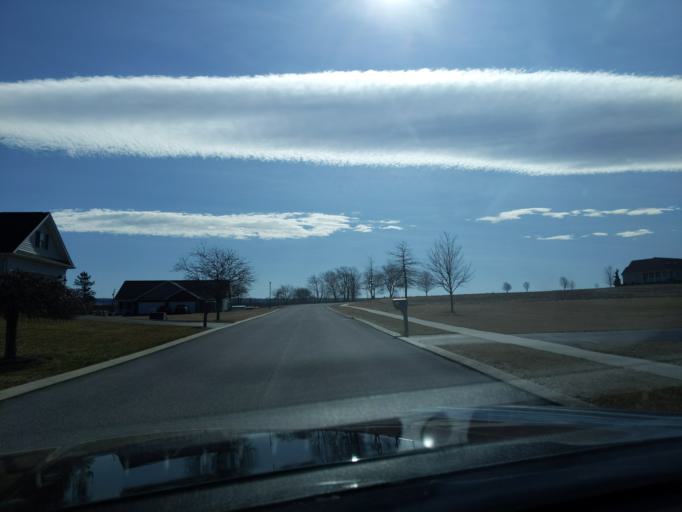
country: US
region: Pennsylvania
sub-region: Blair County
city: Martinsburg
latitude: 40.3039
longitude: -78.3230
